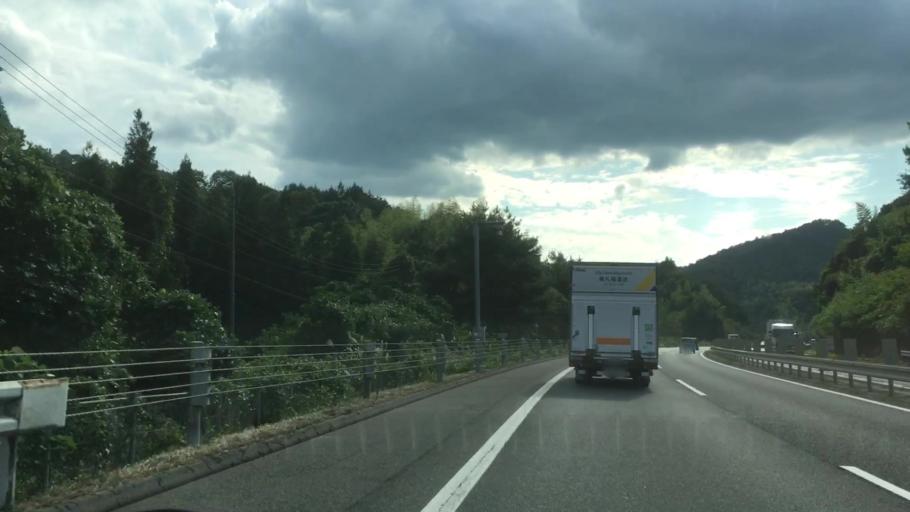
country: JP
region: Yamaguchi
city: Iwakuni
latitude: 34.1430
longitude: 132.1234
